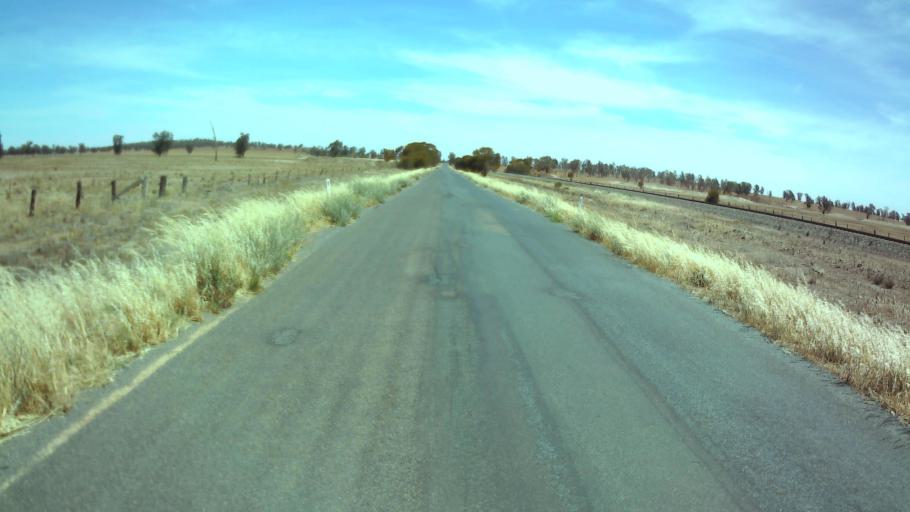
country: AU
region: New South Wales
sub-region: Weddin
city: Grenfell
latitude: -33.7616
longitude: 147.7607
